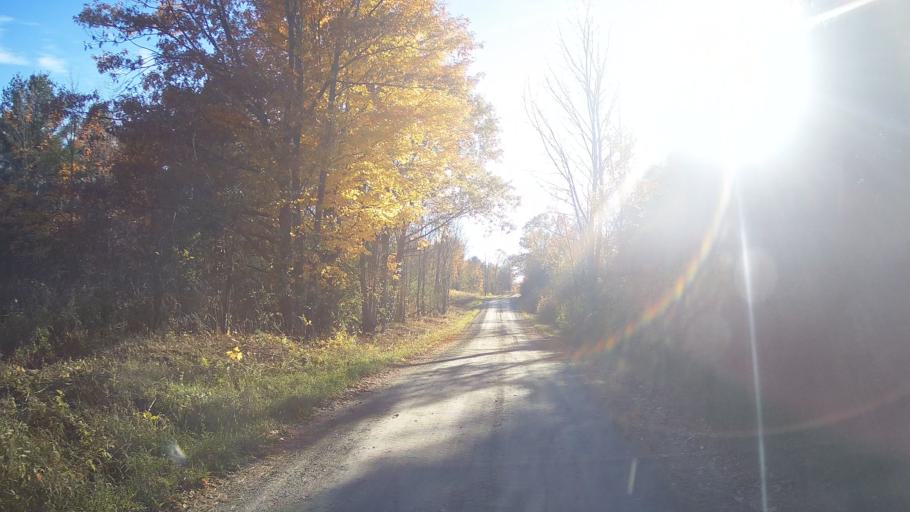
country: CA
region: Ontario
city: Perth
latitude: 44.7162
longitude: -76.4162
